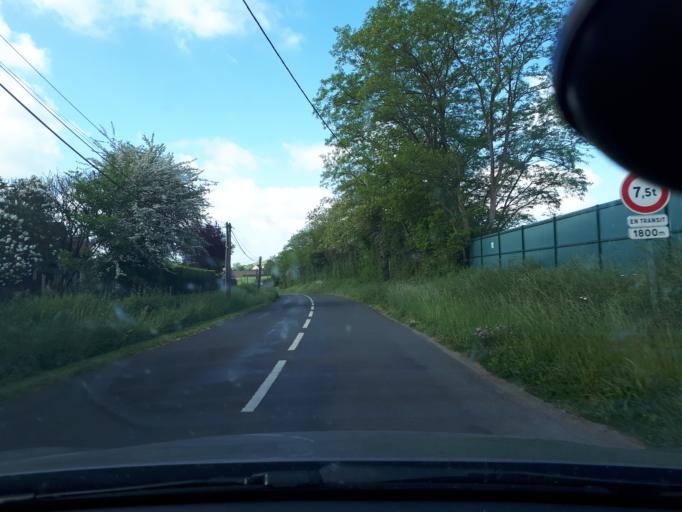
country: FR
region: Pays de la Loire
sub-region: Departement de la Sarthe
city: Champagne
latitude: 48.0355
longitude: 0.2879
